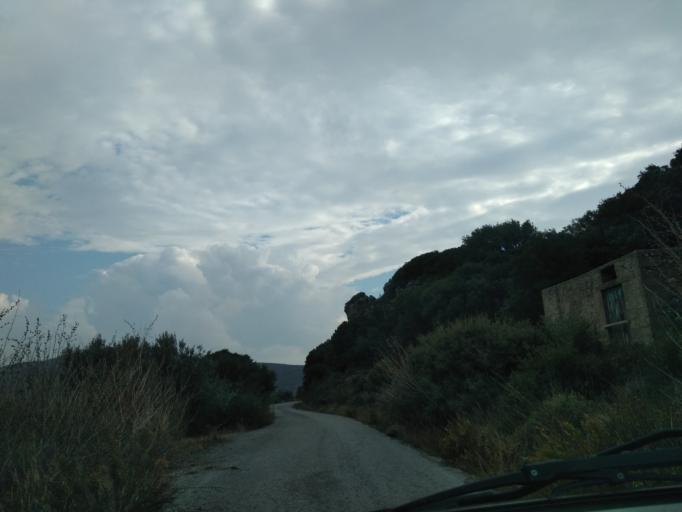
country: GR
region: Crete
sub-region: Nomos Lasithiou
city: Makry-Gialos
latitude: 35.1242
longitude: 26.0215
